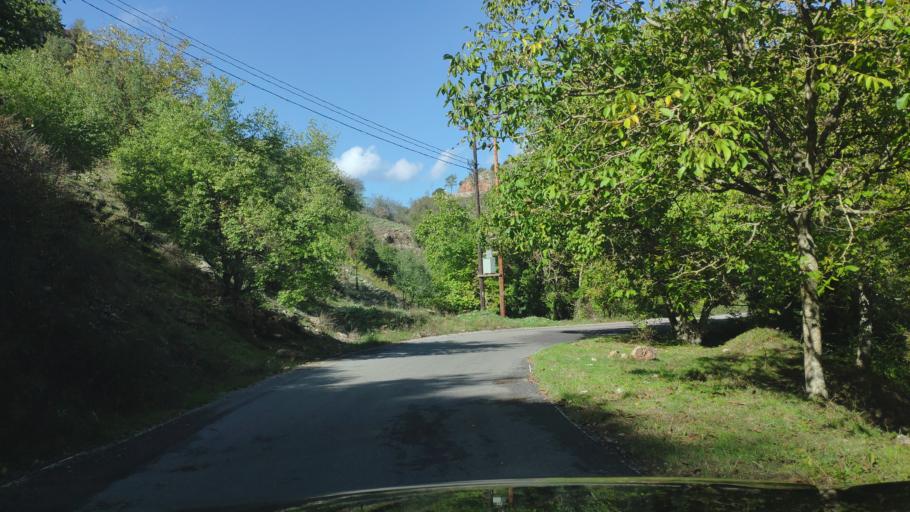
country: GR
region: Peloponnese
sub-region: Nomos Arkadias
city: Dimitsana
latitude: 37.5970
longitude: 22.0393
